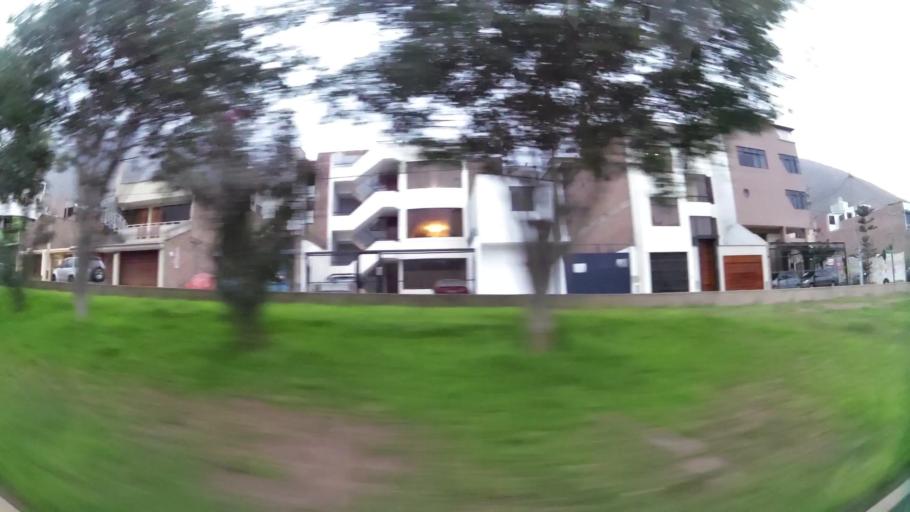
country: PE
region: Lima
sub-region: Lima
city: La Molina
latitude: -12.1152
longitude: -76.9401
